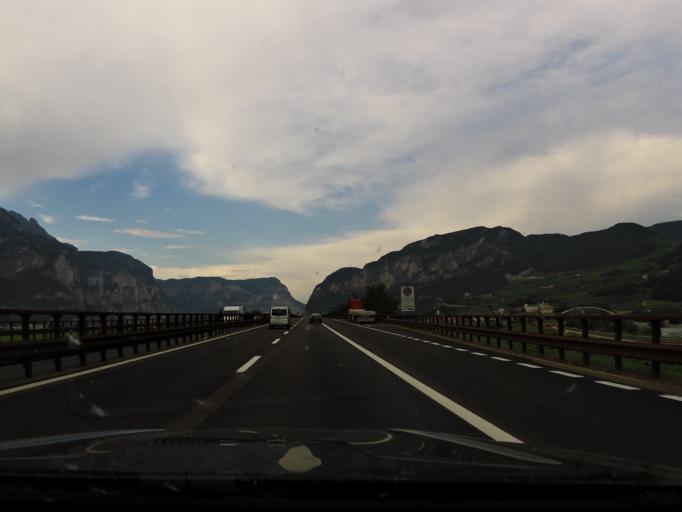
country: IT
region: Trentino-Alto Adige
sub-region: Provincia di Trento
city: San Michele All'Adige
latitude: 46.1898
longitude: 11.1188
